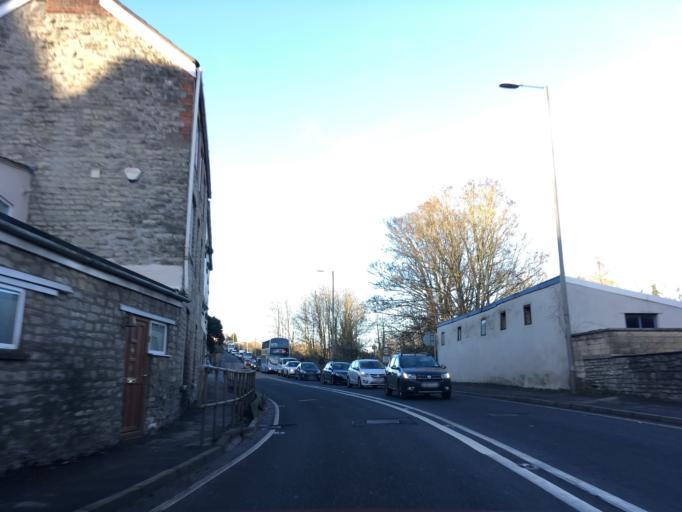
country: GB
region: England
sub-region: Bath and North East Somerset
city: Saltford
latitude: 51.3980
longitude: -2.4498
